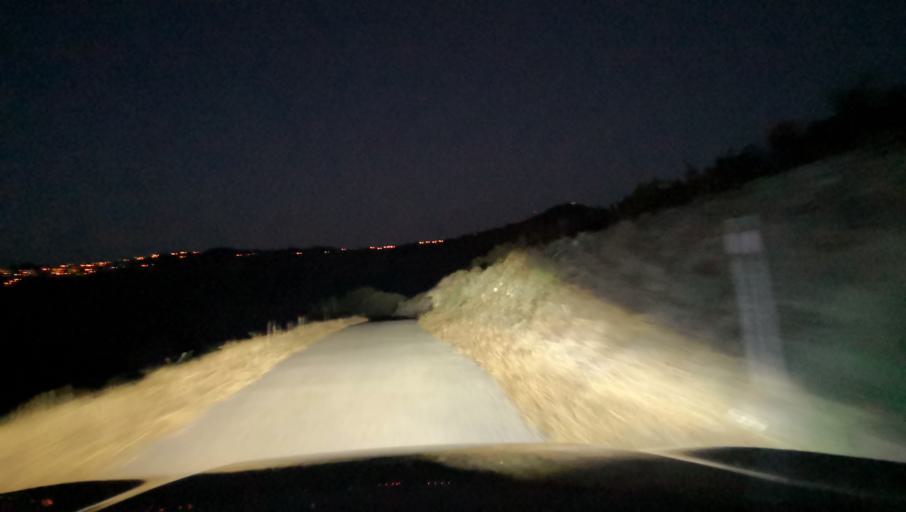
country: PT
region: Viseu
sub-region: Armamar
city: Armamar
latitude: 41.1598
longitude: -7.6966
